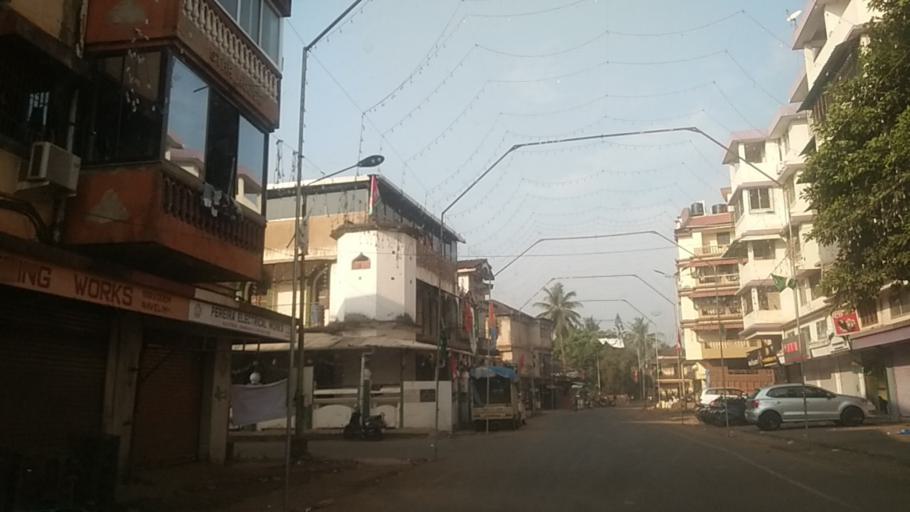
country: IN
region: Goa
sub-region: South Goa
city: Madgaon
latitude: 15.2650
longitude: 73.9604
